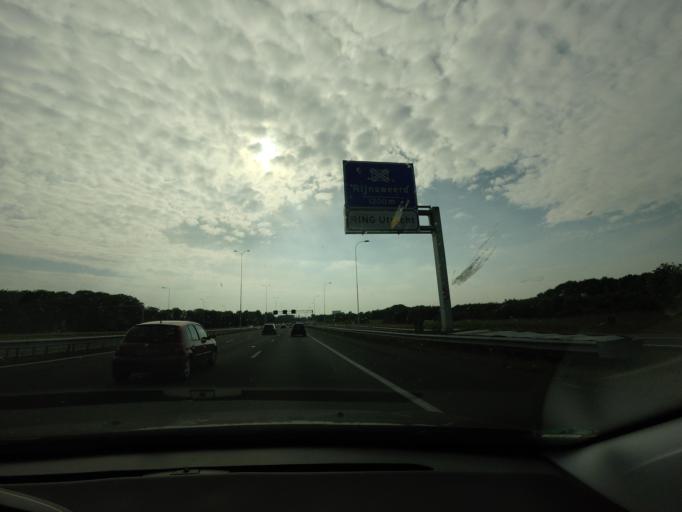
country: NL
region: Utrecht
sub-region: Gemeente De Bilt
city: De Bilt
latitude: 52.0931
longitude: 5.1955
